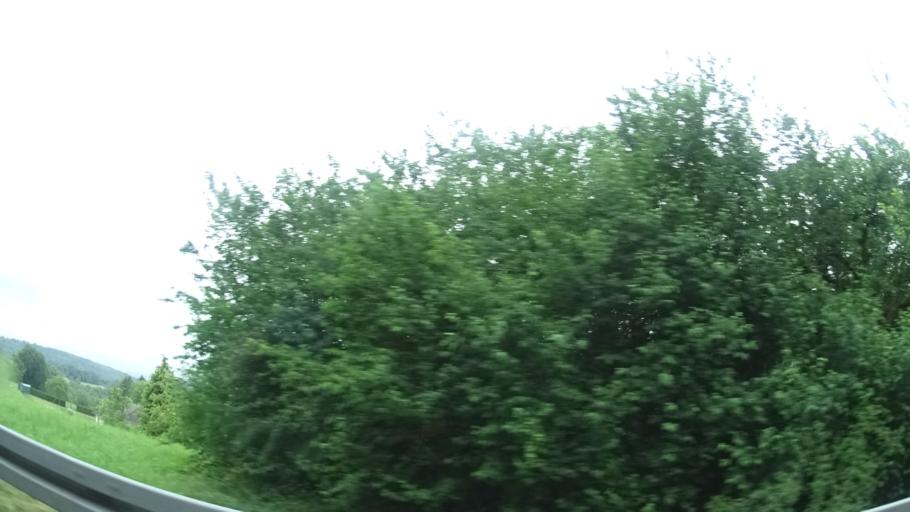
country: DE
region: Saarland
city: Orscholz
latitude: 49.4454
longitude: 6.5485
